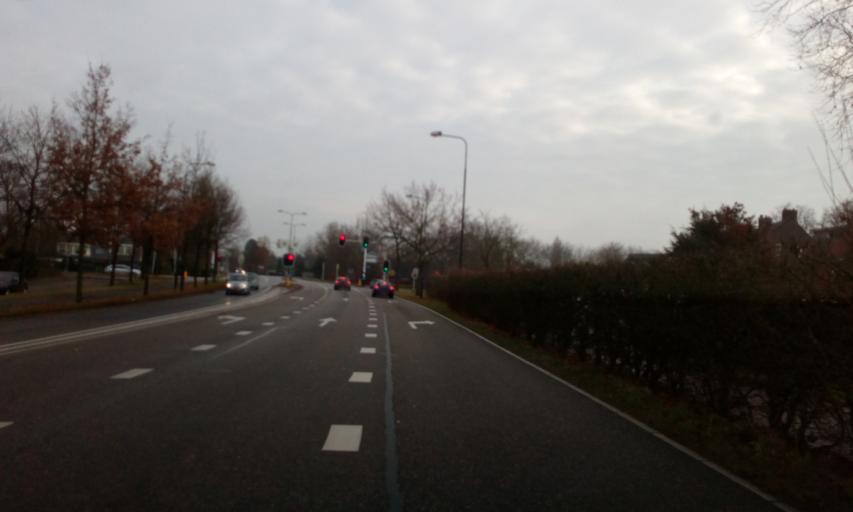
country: NL
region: North Holland
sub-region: Gemeente Naarden
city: Naarden
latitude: 52.2872
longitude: 5.1589
